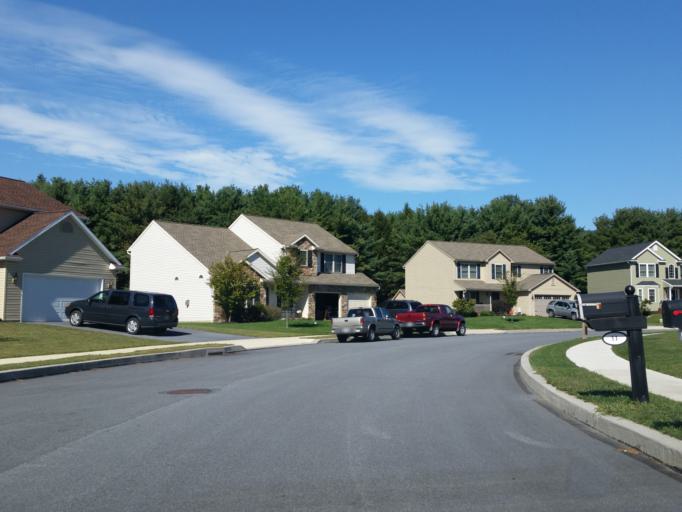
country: US
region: Pennsylvania
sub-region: Lebanon County
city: Jonestown
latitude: 40.4704
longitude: -76.5052
